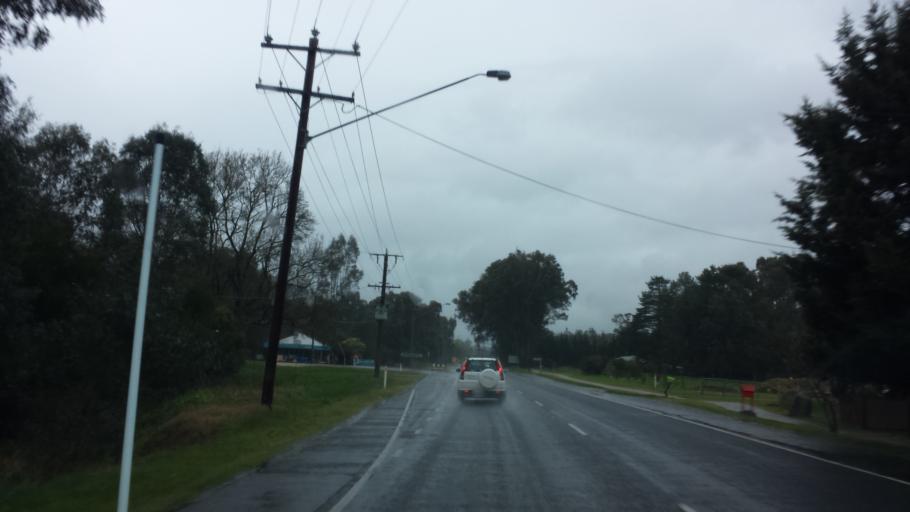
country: AU
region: Victoria
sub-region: Alpine
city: Mount Beauty
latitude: -36.5874
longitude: 146.7600
